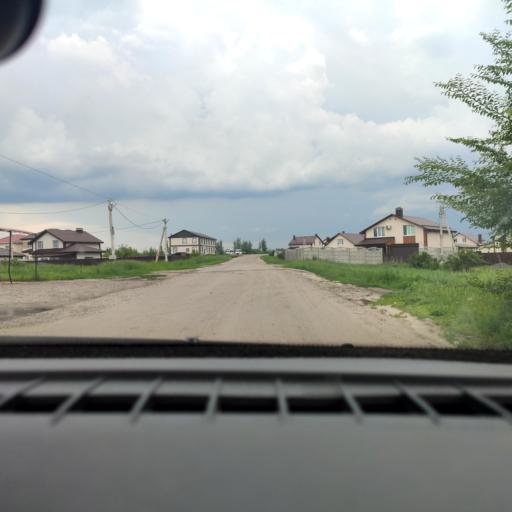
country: RU
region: Voronezj
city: Novaya Usman'
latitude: 51.5998
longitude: 39.3247
